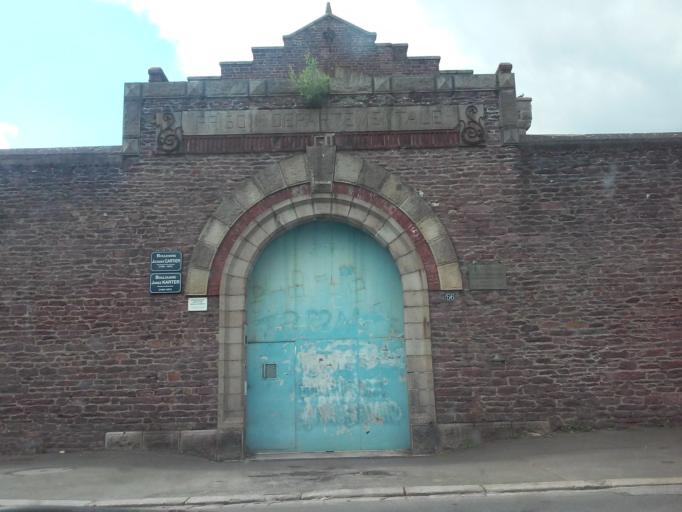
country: FR
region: Brittany
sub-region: Departement d'Ille-et-Vilaine
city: Rennes
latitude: 48.0970
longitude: -1.6837
